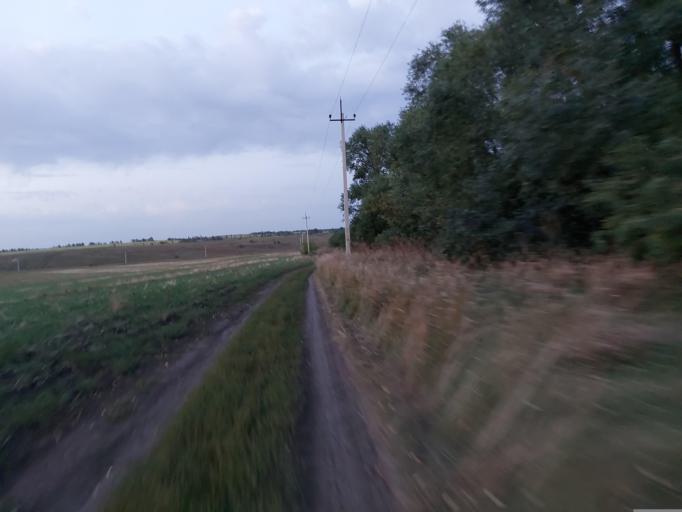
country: RU
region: Lipetsk
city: Dolgorukovo
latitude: 52.3824
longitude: 38.0468
